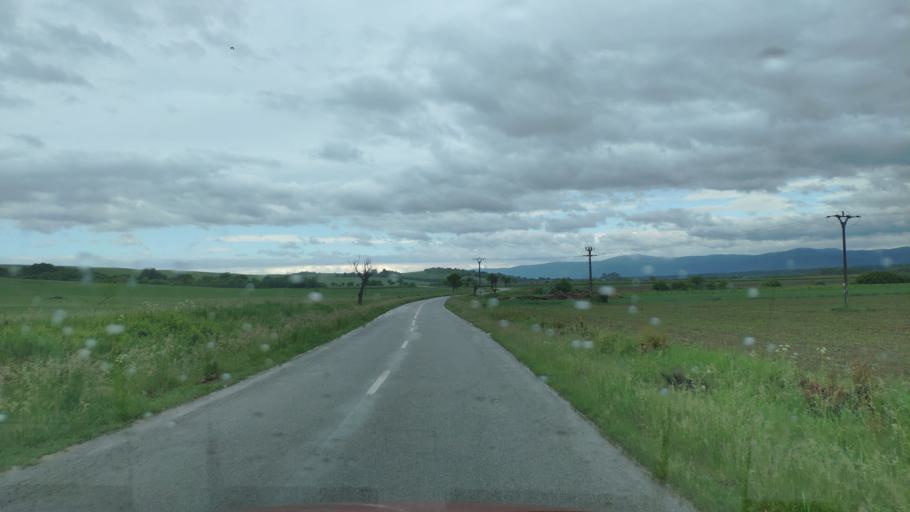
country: SK
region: Kosicky
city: Moldava nad Bodvou
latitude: 48.5377
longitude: 21.0656
